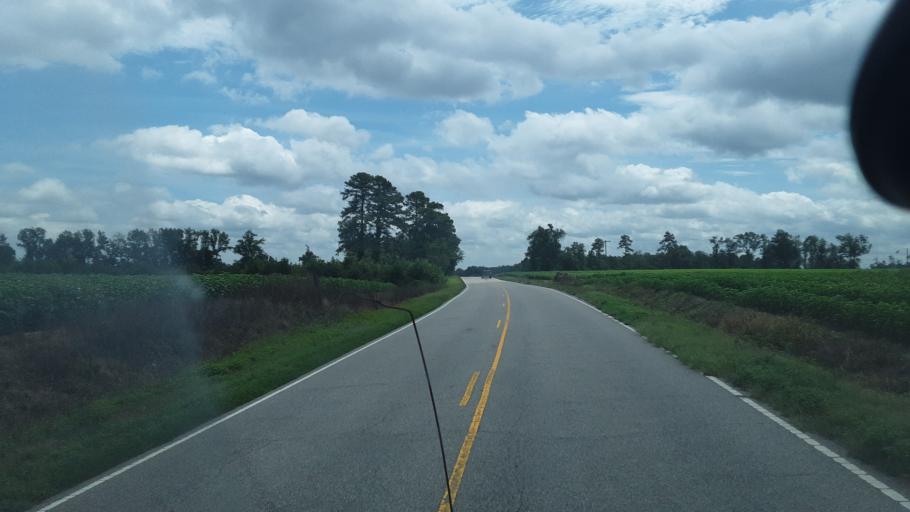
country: US
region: North Carolina
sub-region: Robeson County
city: Fairmont
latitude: 34.3756
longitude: -79.1115
